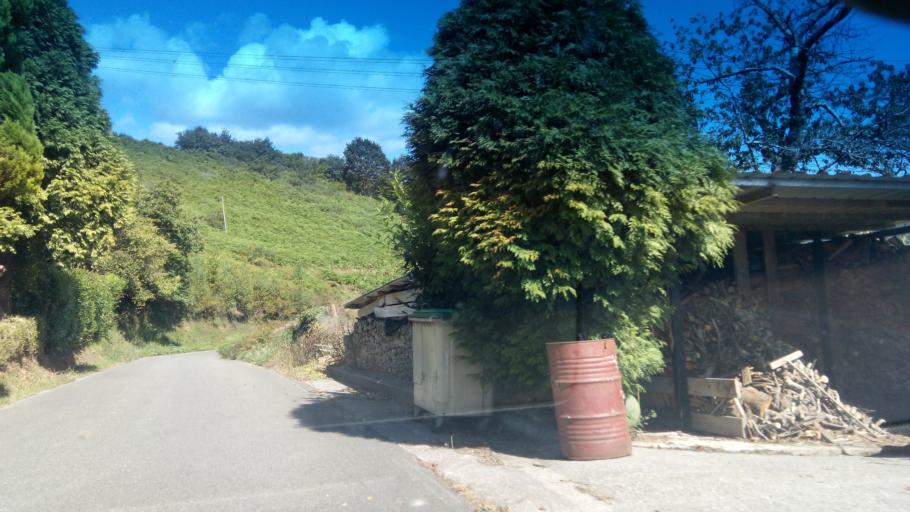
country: ES
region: Asturias
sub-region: Province of Asturias
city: Parres
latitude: 43.3724
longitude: -5.1727
